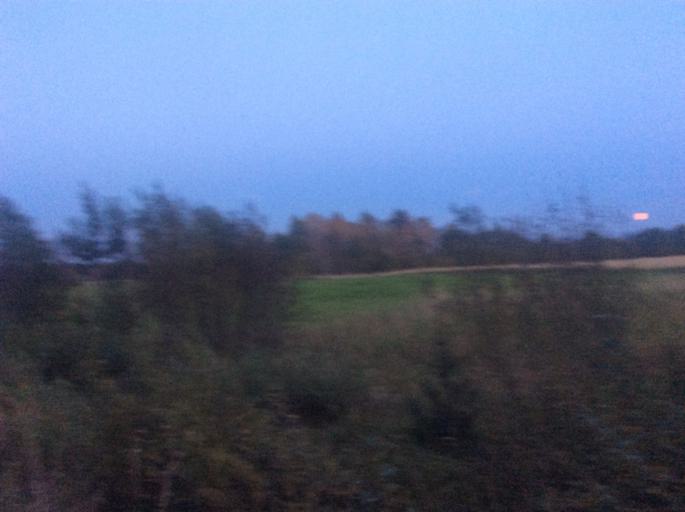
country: RU
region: Vologda
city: Ferapontovo
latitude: 59.9633
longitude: 38.5906
